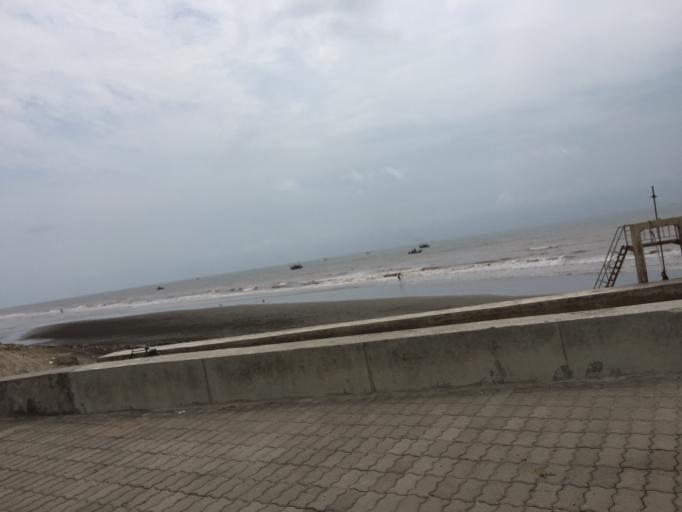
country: VN
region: Ninh Binh
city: Thi Tran Phat Diem
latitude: 20.0349
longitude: 106.2272
